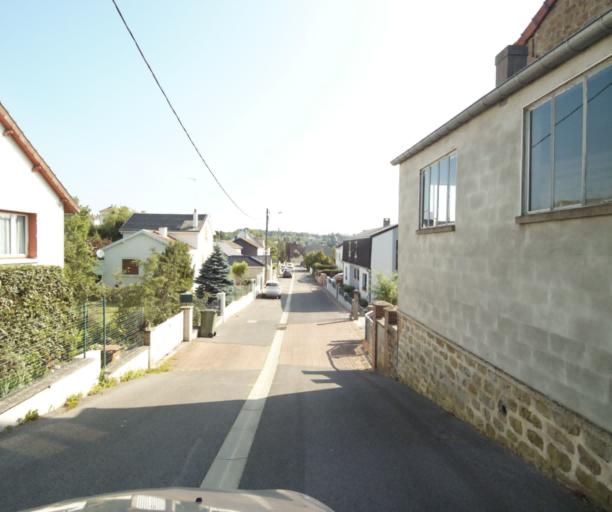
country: FR
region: Champagne-Ardenne
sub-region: Departement des Ardennes
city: Charleville-Mezieres
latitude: 49.7770
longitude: 4.7061
